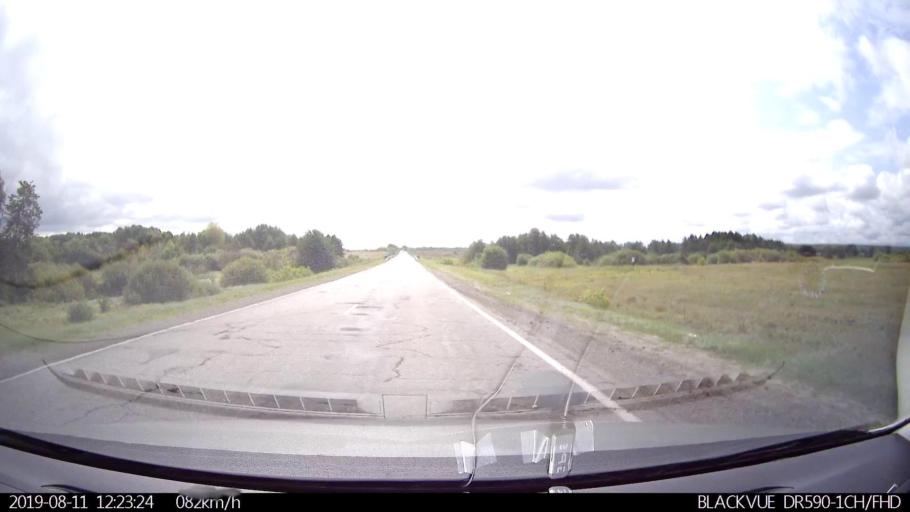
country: RU
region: Ulyanovsk
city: Ignatovka
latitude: 53.8959
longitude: 47.9505
